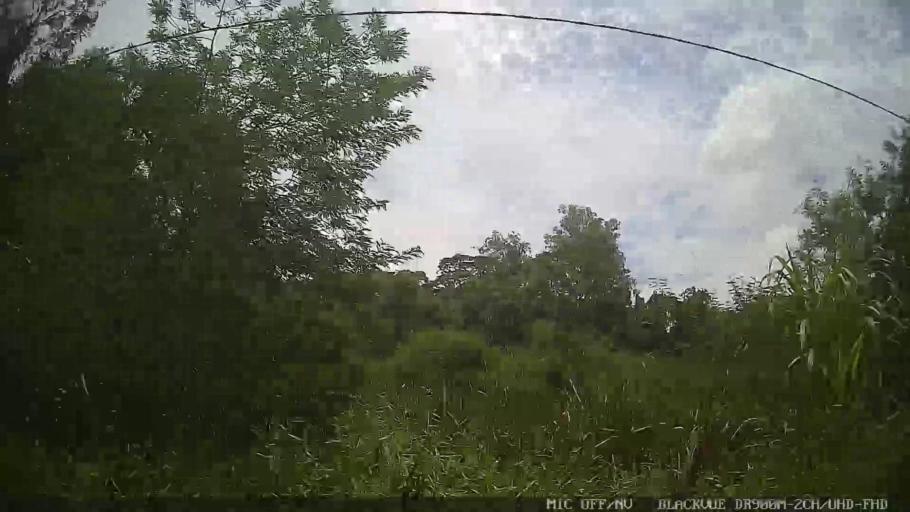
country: BR
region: Sao Paulo
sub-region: Santa Isabel
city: Santa Isabel
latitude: -23.3483
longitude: -46.2248
